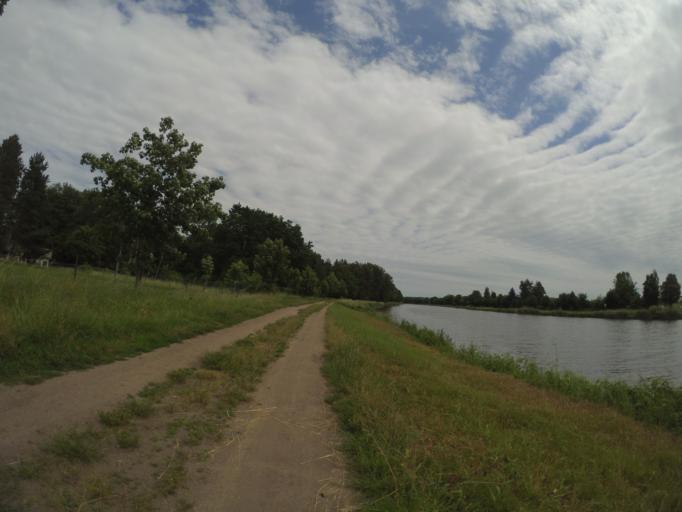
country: CZ
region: Central Bohemia
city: Celakovice
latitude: 50.1730
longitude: 14.7803
